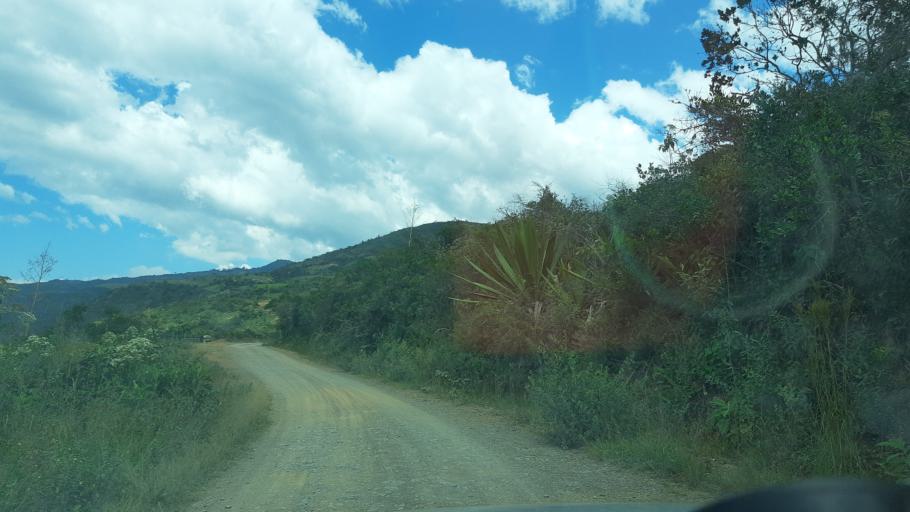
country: CO
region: Boyaca
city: Santa Sofia
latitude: 5.6940
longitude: -73.5693
